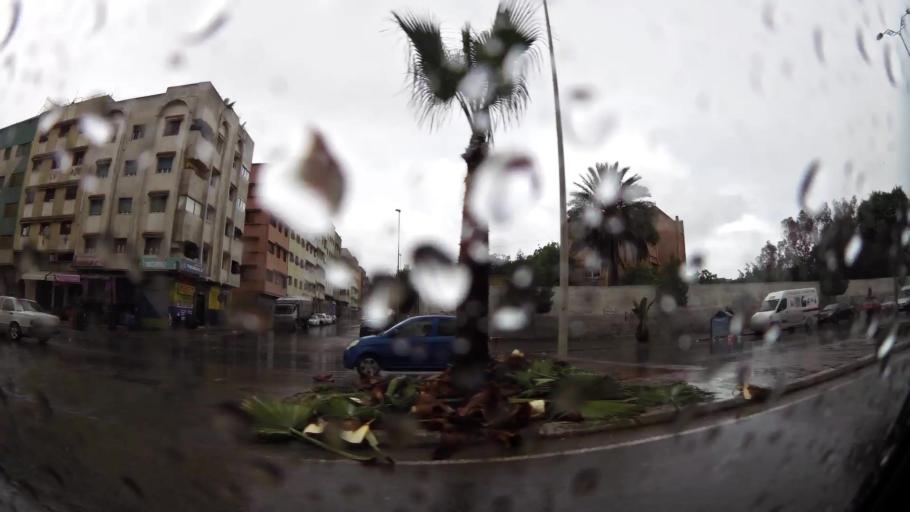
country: MA
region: Grand Casablanca
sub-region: Casablanca
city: Casablanca
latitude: 33.5378
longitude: -7.5721
